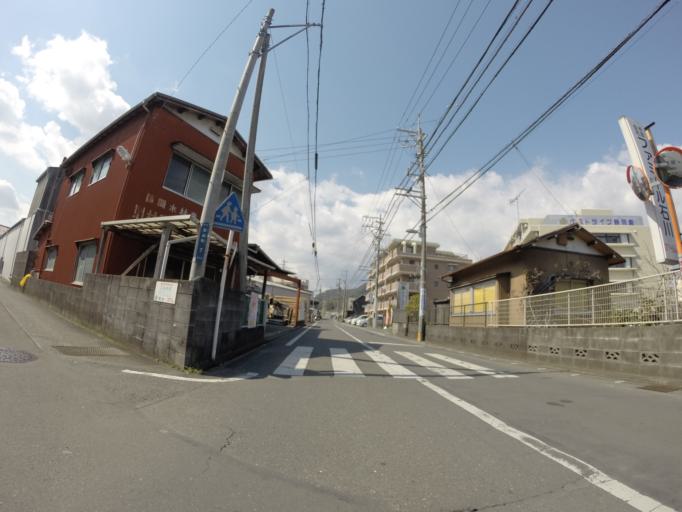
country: JP
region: Shizuoka
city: Shizuoka-shi
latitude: 34.9866
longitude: 138.3657
